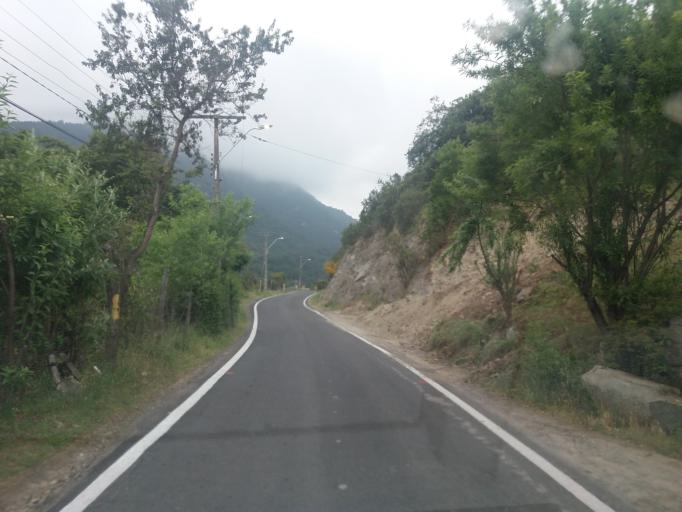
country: CL
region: Valparaiso
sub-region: Provincia de Marga Marga
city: Limache
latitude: -33.0437
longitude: -71.0988
